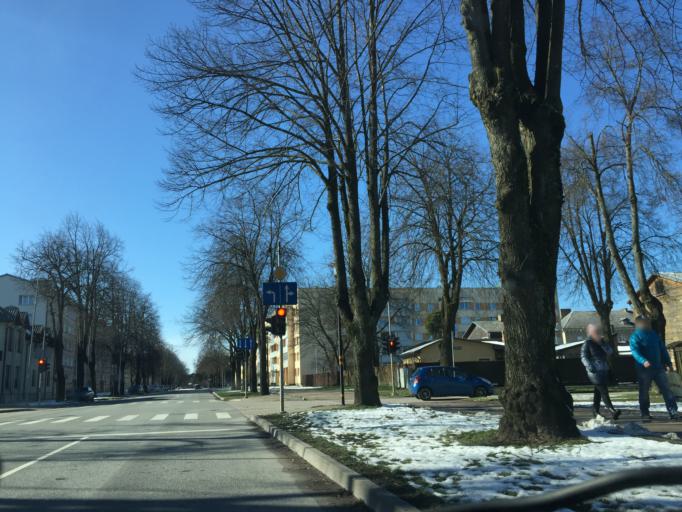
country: LV
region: Ventspils
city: Ventspils
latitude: 57.3897
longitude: 21.5545
